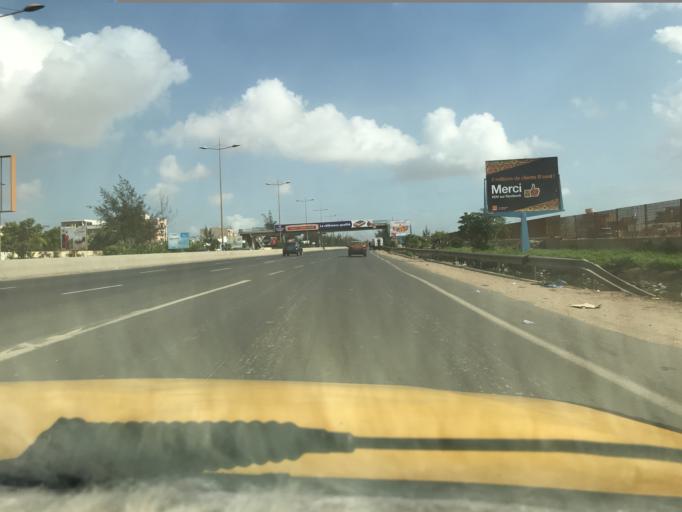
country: SN
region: Dakar
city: Dakar
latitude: 14.6997
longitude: -17.4420
